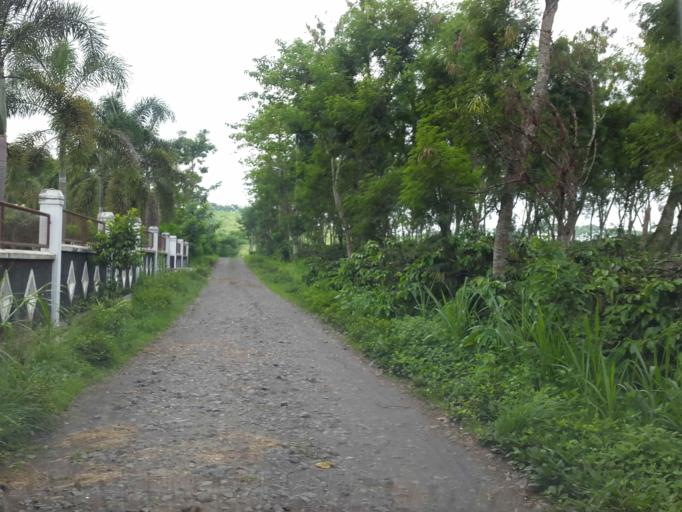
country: ID
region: East Java
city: Pandansari
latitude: -8.0857
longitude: 112.7933
